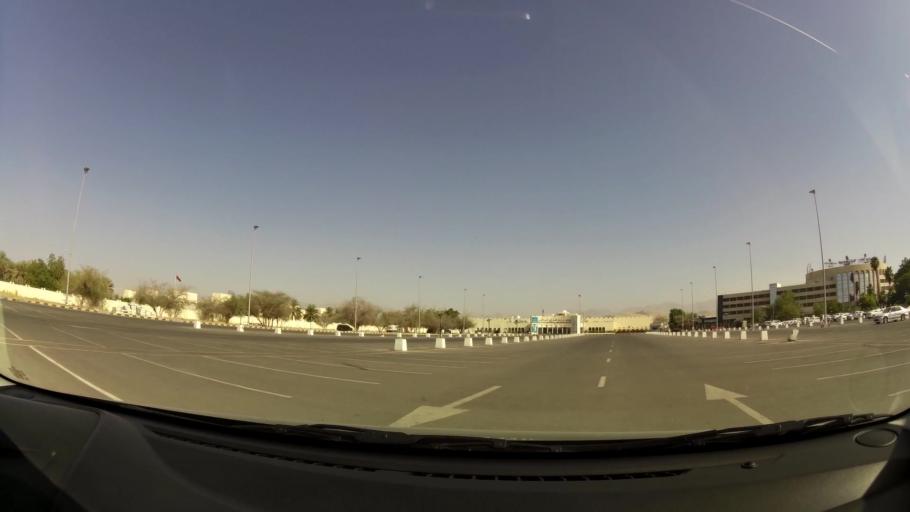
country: OM
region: Muhafazat Masqat
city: Bawshar
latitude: 23.5865
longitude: 58.3048
